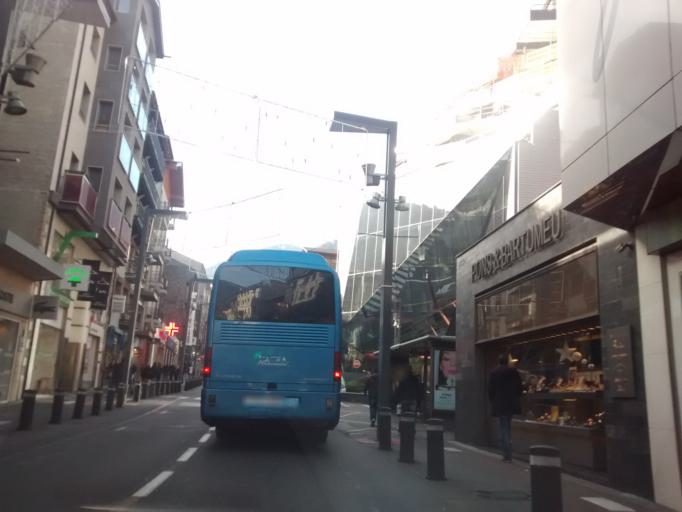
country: AD
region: Andorra la Vella
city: Andorra la Vella
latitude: 42.5084
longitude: 1.5263
